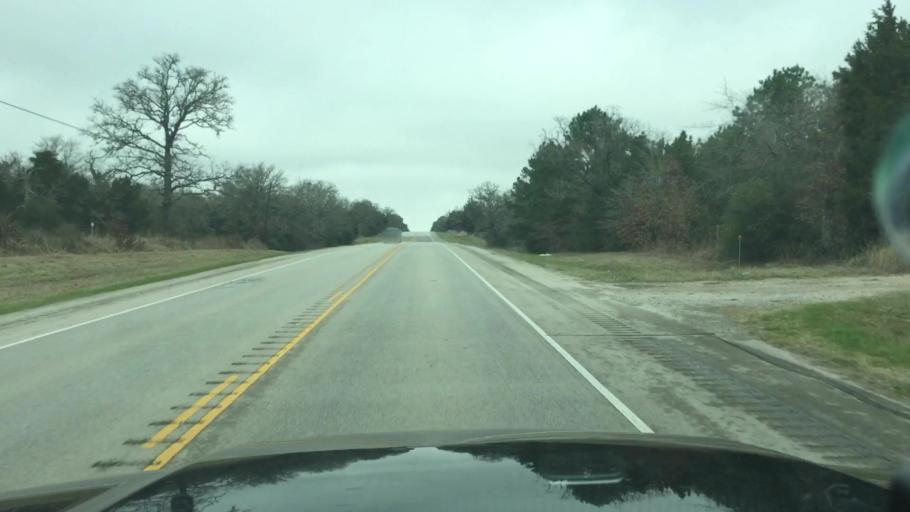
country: US
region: Texas
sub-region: Lee County
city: Giddings
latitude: 30.0731
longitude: -96.9169
